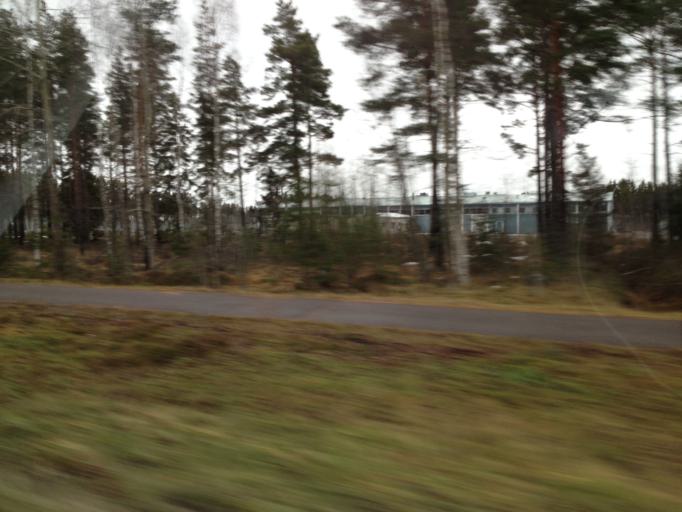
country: FI
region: Uusimaa
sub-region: Raaseporin
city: Hanko
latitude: 59.8452
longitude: 23.0074
